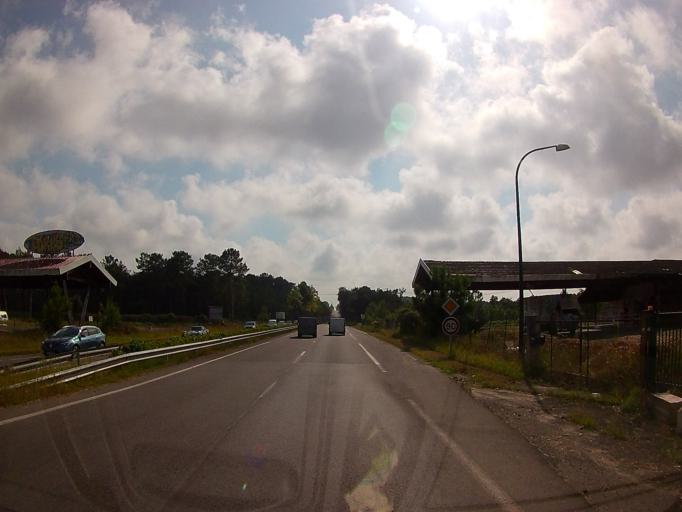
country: FR
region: Aquitaine
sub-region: Departement des Landes
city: Ondres
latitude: 43.5779
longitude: -1.4358
